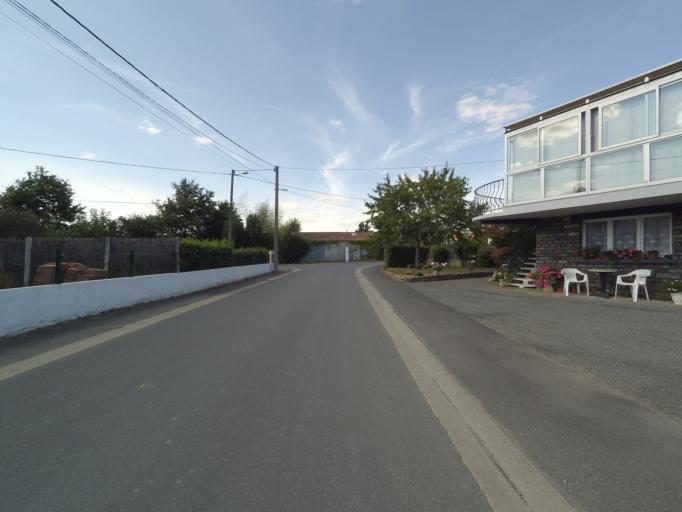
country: FR
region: Pays de la Loire
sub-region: Departement de la Loire-Atlantique
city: Vieillevigne
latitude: 46.9661
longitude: -1.4412
